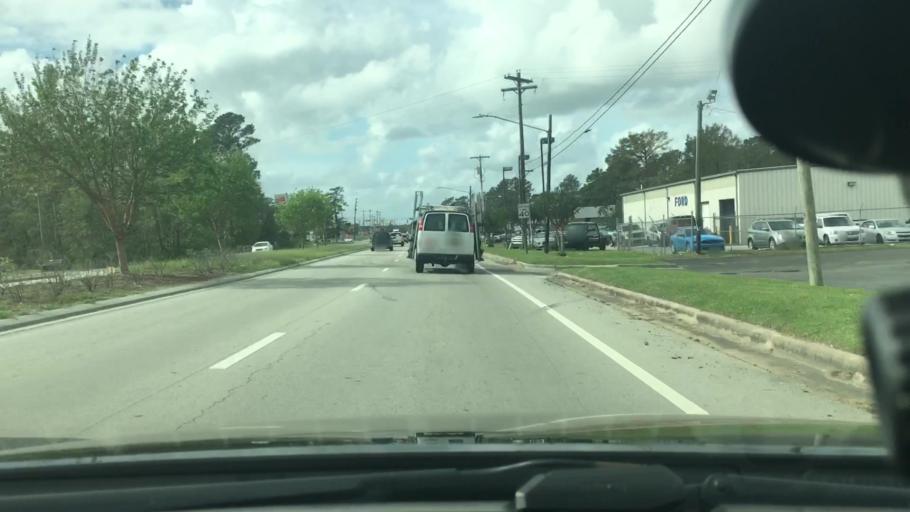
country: US
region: North Carolina
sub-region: Craven County
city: Havelock
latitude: 34.8812
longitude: -76.9074
